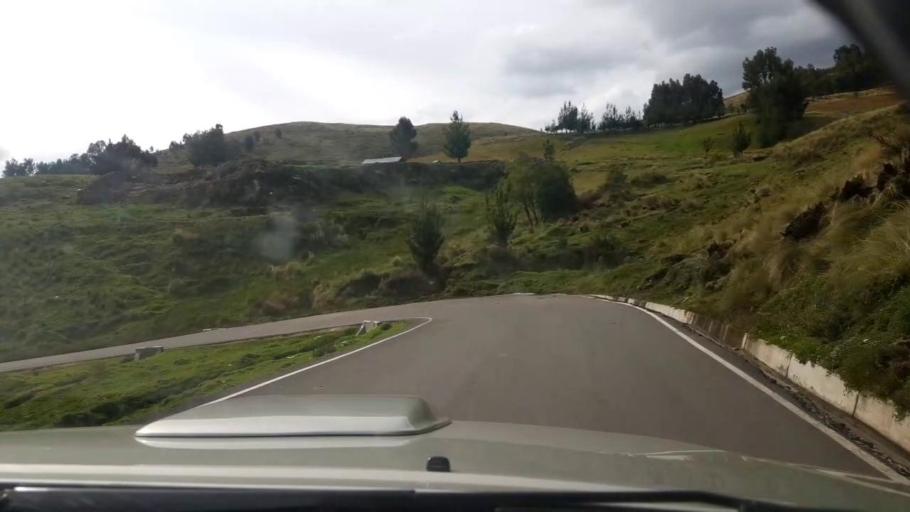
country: PE
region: Ayacucho
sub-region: Provincia de Cangallo
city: Pampa Cangallo
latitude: -13.4502
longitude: -74.2021
